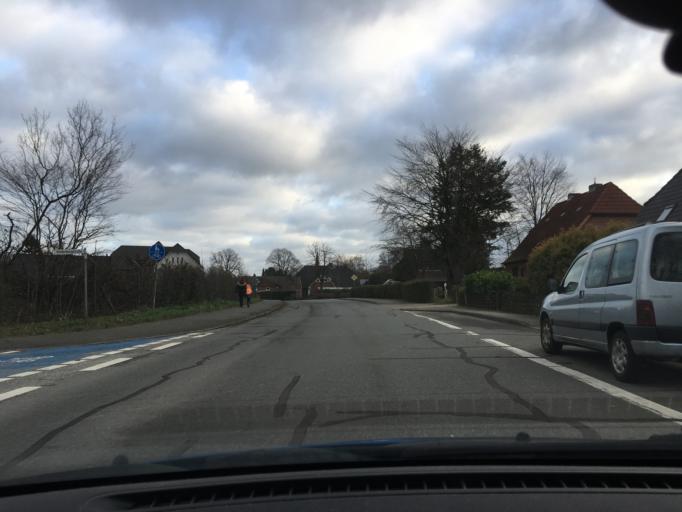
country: DE
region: Schleswig-Holstein
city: Schenefeld
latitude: 54.0475
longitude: 9.4759
